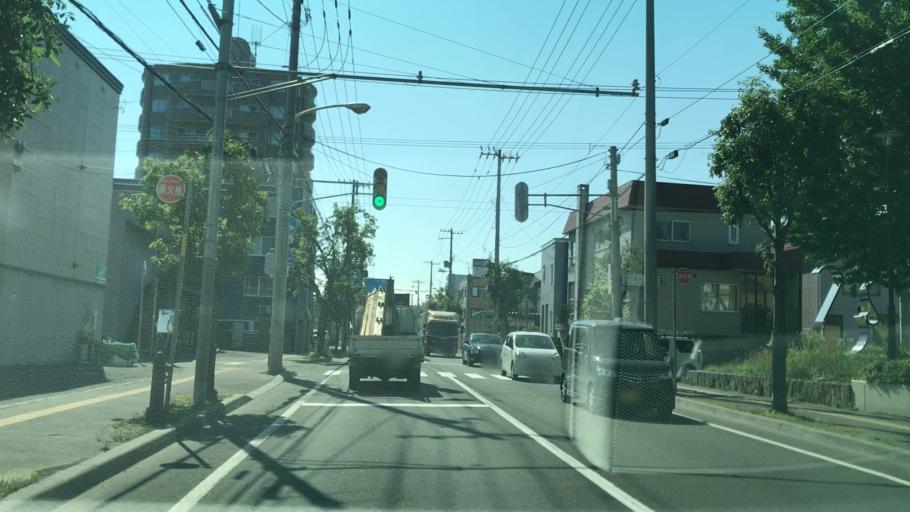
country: JP
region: Hokkaido
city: Sapporo
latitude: 43.0550
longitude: 141.4065
